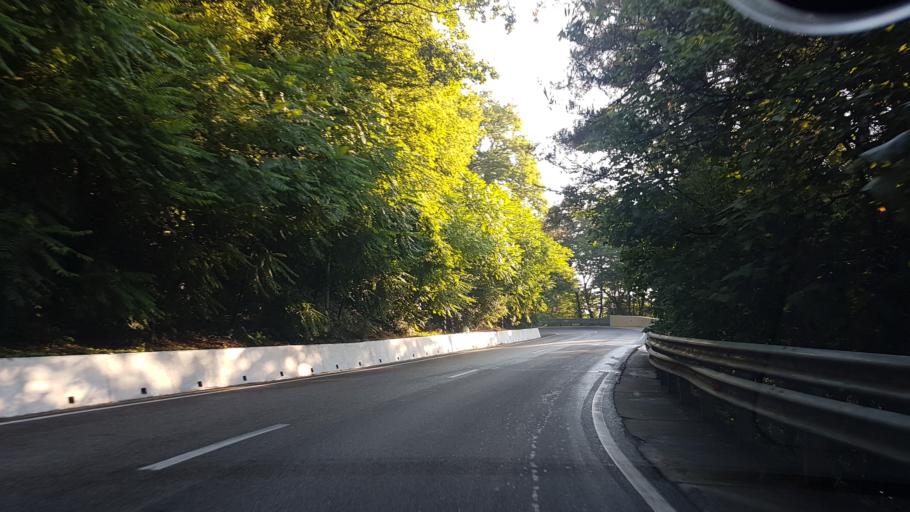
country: RU
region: Krasnodarskiy
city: Dagomys
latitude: 43.6449
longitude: 39.6959
